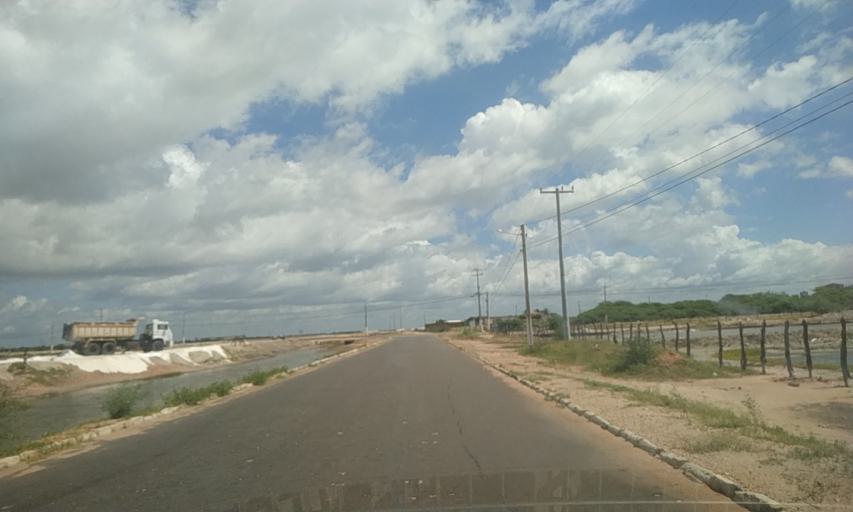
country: BR
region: Rio Grande do Norte
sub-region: Areia Branca
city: Areia Branca
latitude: -4.9348
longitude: -37.1127
